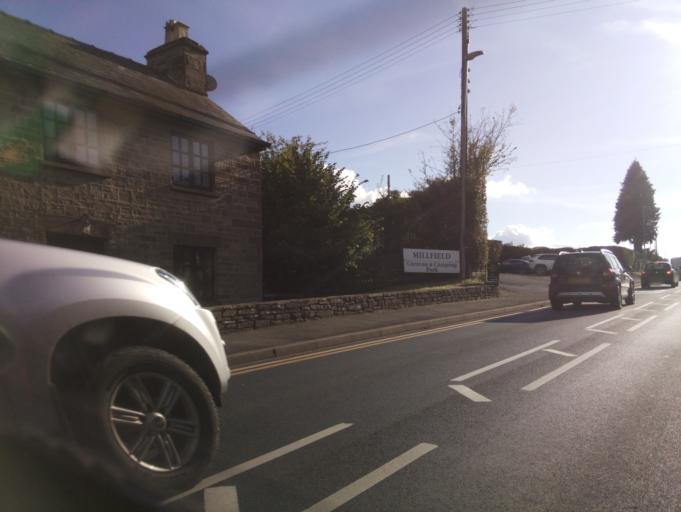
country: GB
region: Wales
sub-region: Sir Powys
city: Hay
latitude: 52.0324
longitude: -3.2061
